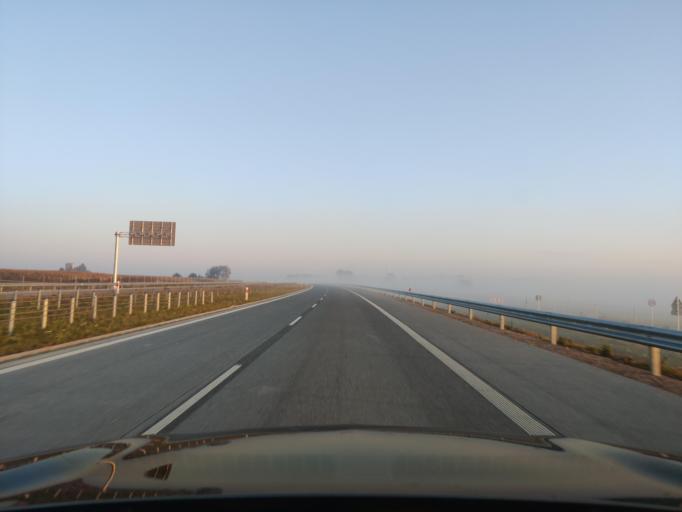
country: PL
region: Masovian Voivodeship
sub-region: Powiat mlawski
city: Wisniewo
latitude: 52.9970
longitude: 20.3456
